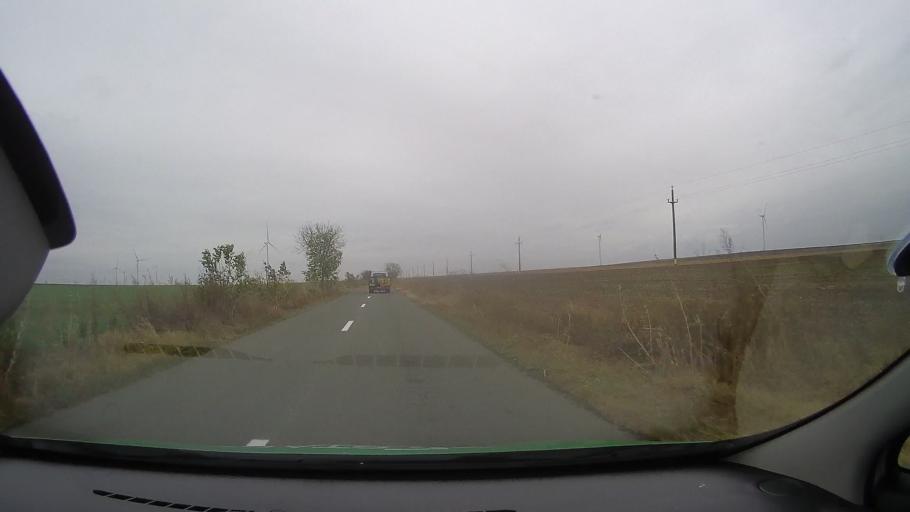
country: RO
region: Constanta
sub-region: Comuna Targusor
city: Targusor
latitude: 44.4735
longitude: 28.3836
